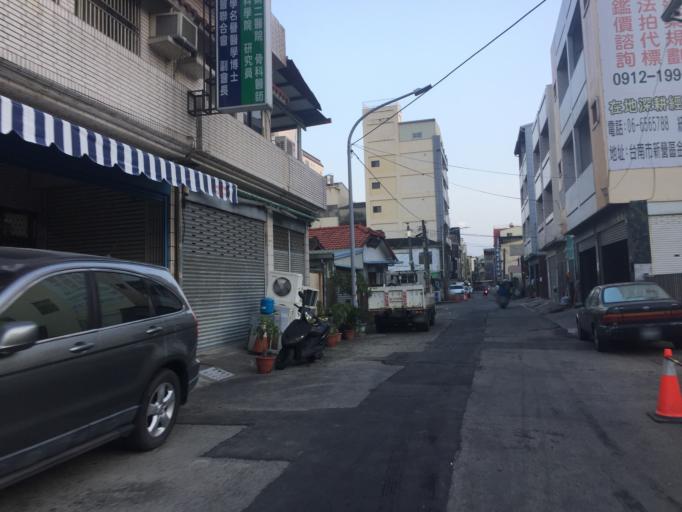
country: TW
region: Taiwan
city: Xinying
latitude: 23.3059
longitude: 120.3136
